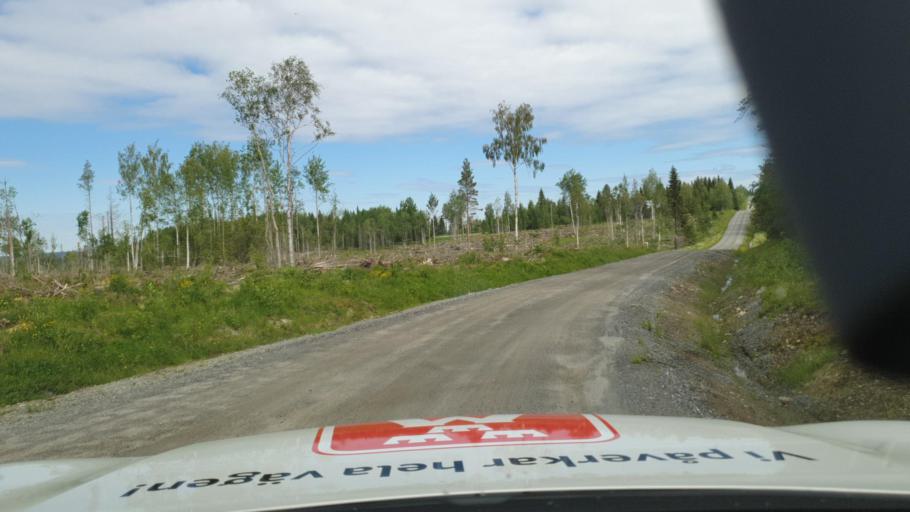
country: SE
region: Vaesterbotten
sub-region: Skelleftea Kommun
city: Langsele
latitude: 64.6281
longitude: 20.2493
